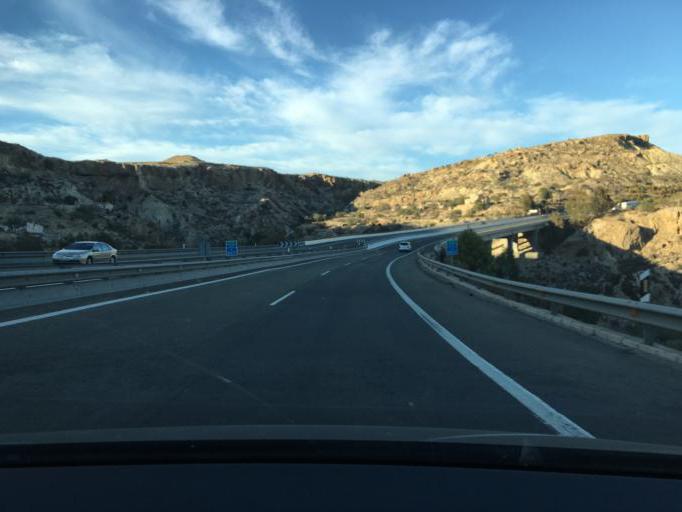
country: ES
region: Andalusia
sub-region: Provincia de Almeria
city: Sorbas
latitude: 37.0906
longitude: -2.0636
